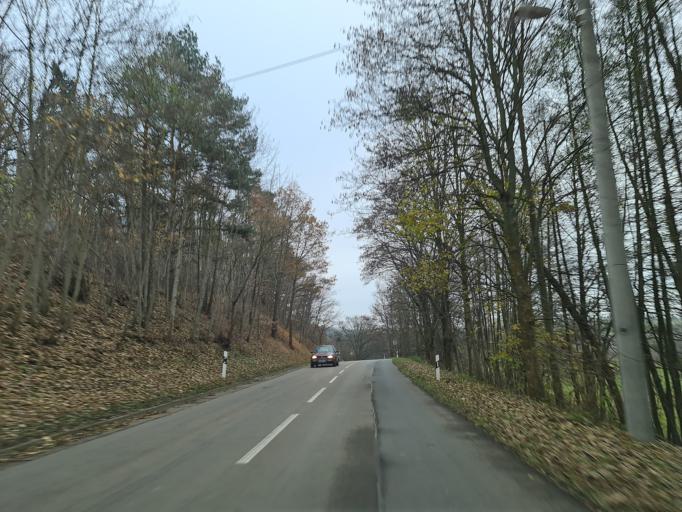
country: DE
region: Saxony
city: Syrau
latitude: 50.5099
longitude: 12.0928
